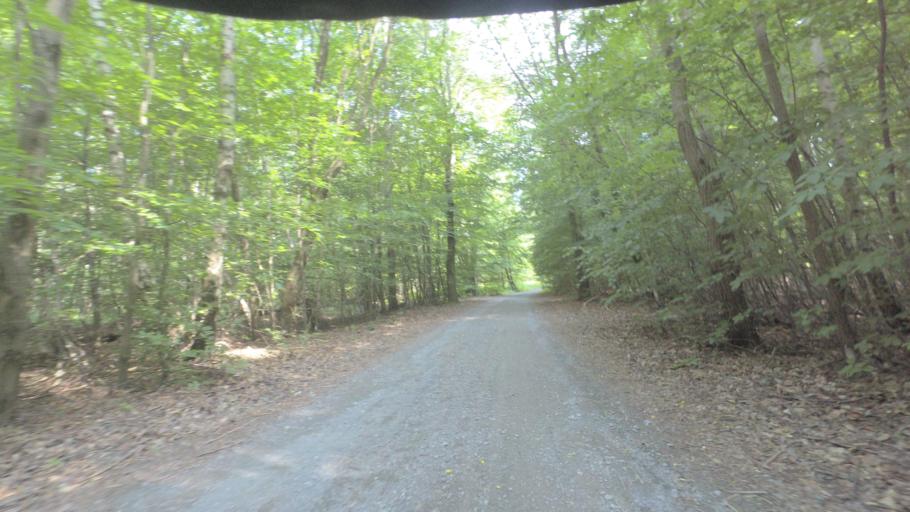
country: DE
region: Saxony-Anhalt
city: Stapelburg
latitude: 51.8828
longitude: 10.6523
